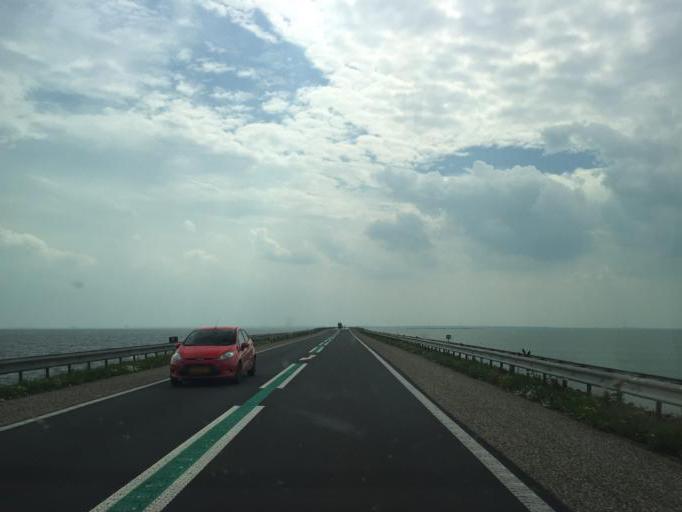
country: NL
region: Flevoland
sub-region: Gemeente Lelystad
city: Lelystad
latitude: 52.6316
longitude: 5.4172
